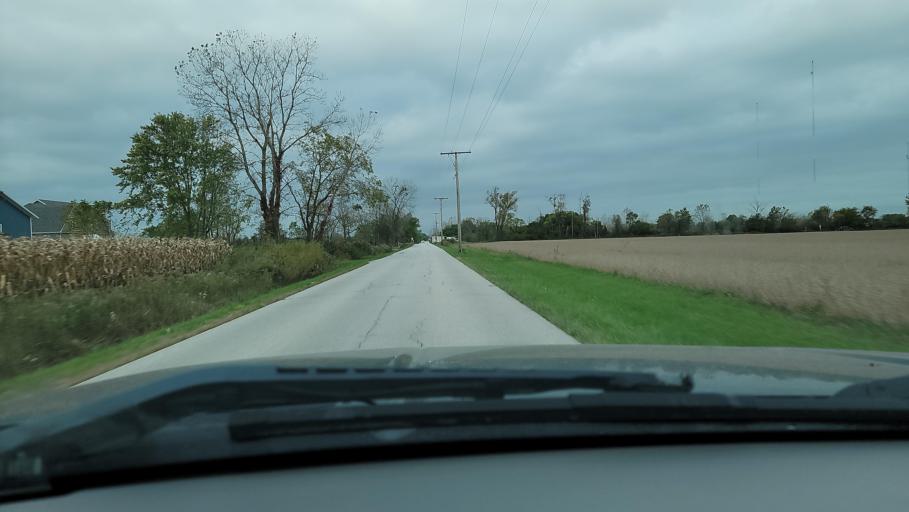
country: US
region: Indiana
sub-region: Porter County
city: South Haven
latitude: 41.5613
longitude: -87.1501
